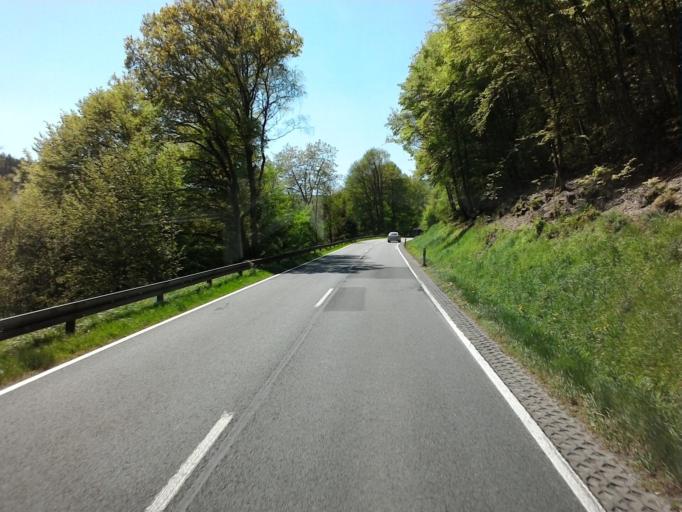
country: DE
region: Bavaria
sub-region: Regierungsbezirk Unterfranken
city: Rechtenbach
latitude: 49.9761
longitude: 9.5377
